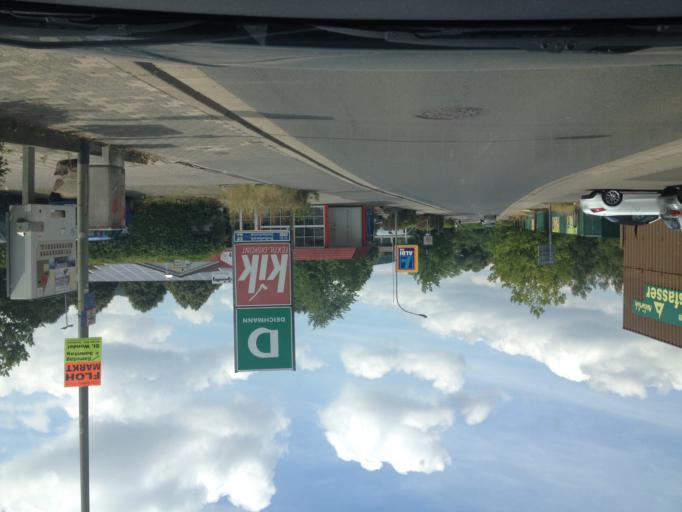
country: DE
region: Saarland
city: Sankt Wendel
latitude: 49.4699
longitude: 7.1699
